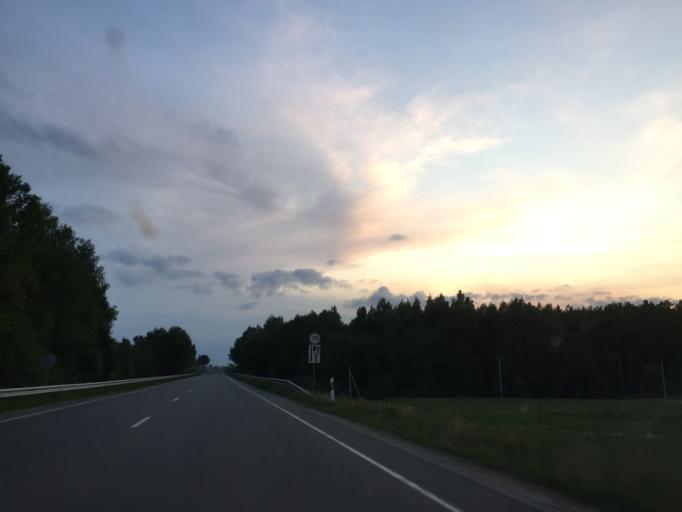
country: LT
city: Vieksniai
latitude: 55.9971
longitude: 22.5063
